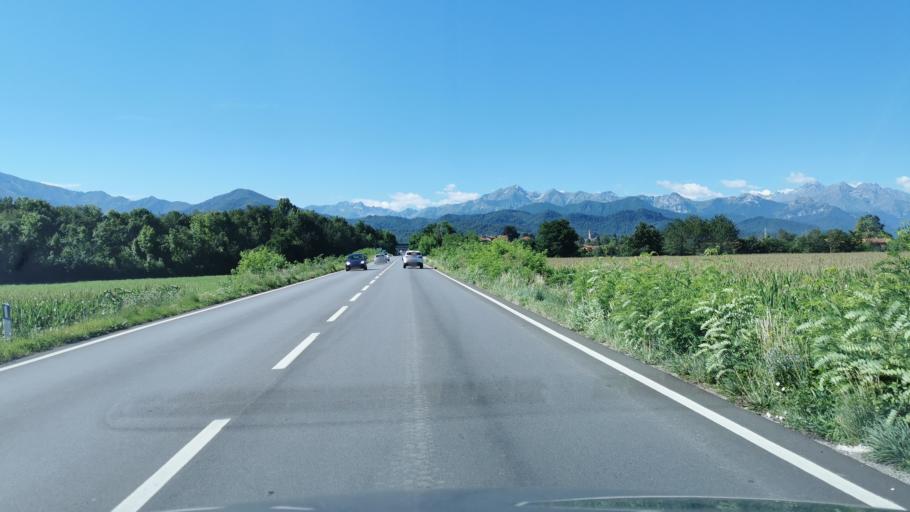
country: IT
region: Piedmont
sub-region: Provincia di Cuneo
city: Cuneo
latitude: 44.3616
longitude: 7.5500
